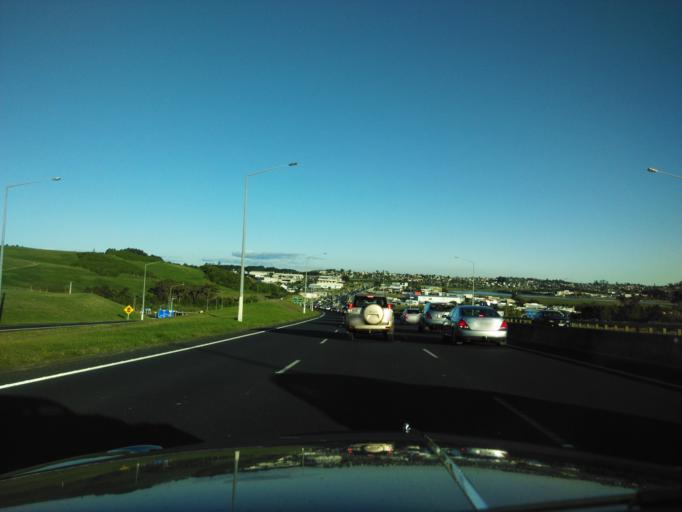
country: NZ
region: Auckland
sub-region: Auckland
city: Rothesay Bay
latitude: -36.7316
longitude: 174.7158
